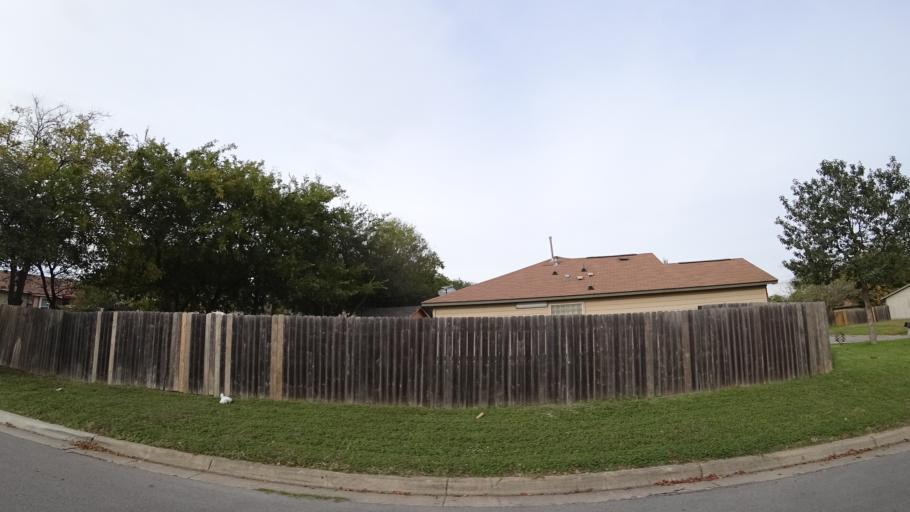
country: US
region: Texas
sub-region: Williamson County
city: Round Rock
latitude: 30.4973
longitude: -97.6646
